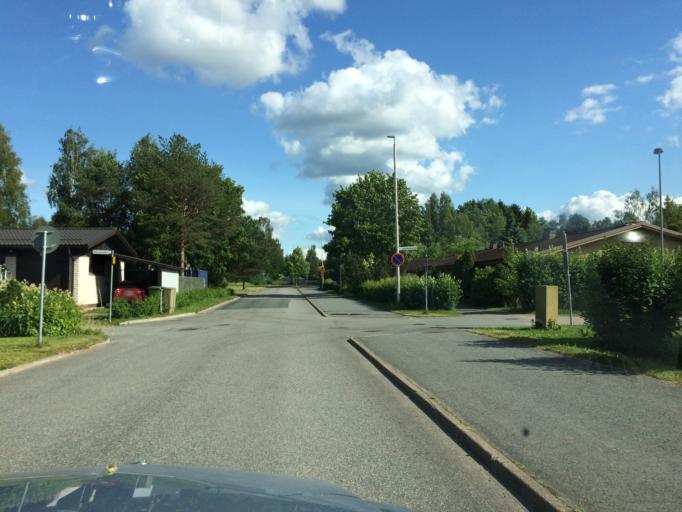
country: FI
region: Haeme
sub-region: Haemeenlinna
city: Haemeenlinna
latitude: 60.9866
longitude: 24.3962
